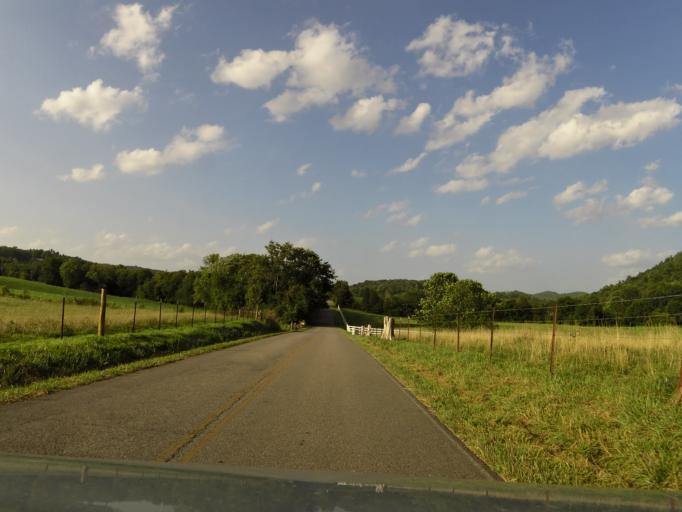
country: US
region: Tennessee
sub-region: Blount County
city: Wildwood
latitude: 35.8341
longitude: -83.8736
